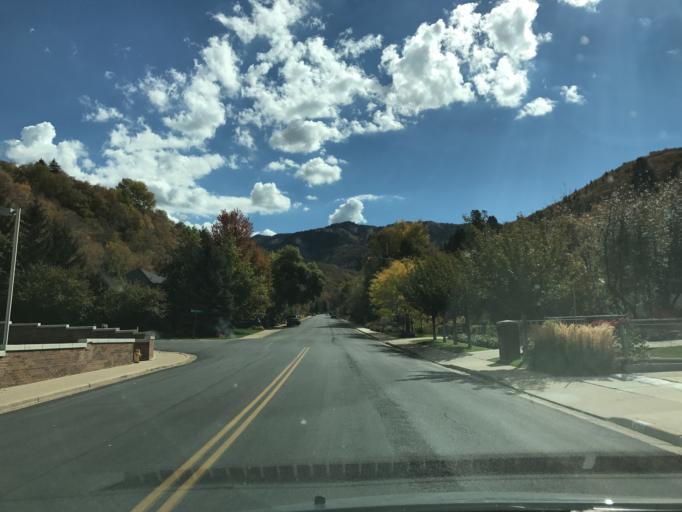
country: US
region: Utah
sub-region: Davis County
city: Bountiful
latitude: 40.8664
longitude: -111.8429
